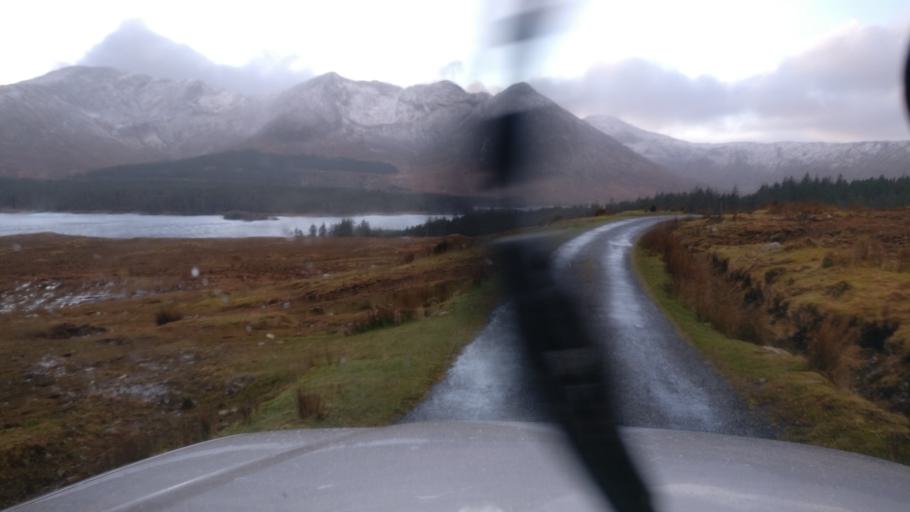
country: IE
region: Connaught
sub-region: County Galway
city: Clifden
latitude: 53.5182
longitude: -9.7304
